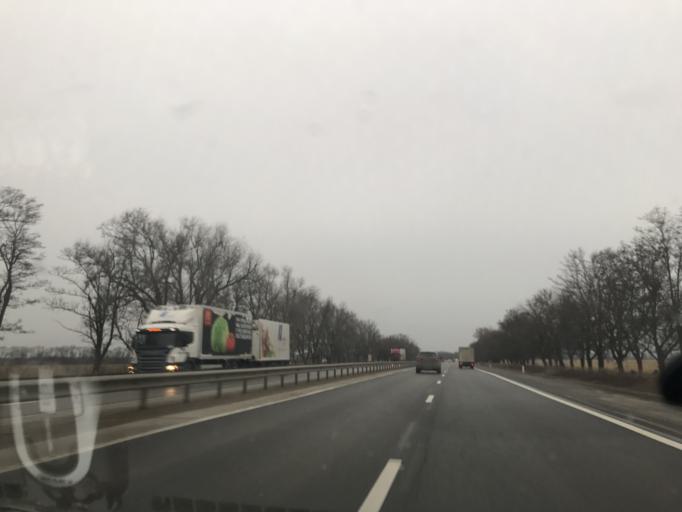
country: RU
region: Krasnodarskiy
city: Pavlovskaya
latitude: 46.1757
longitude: 39.8371
